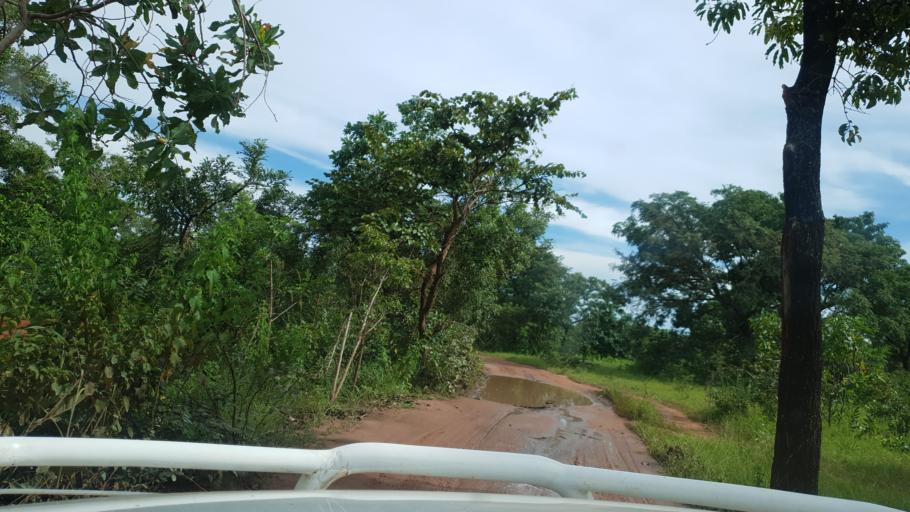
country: ML
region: Sikasso
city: Kolondieba
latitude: 10.7478
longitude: -6.9126
